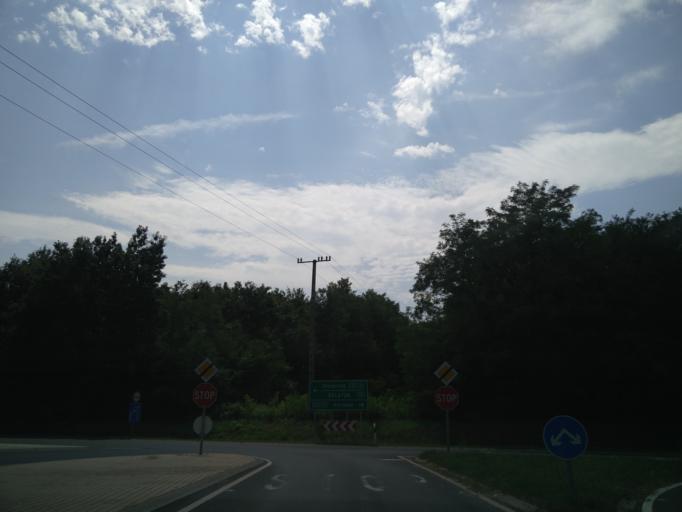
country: HU
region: Zala
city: Zalaegerszeg
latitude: 46.8758
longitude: 16.8527
